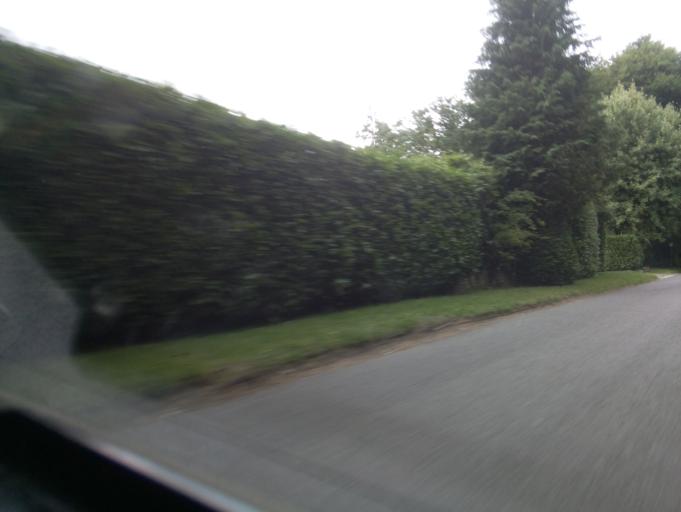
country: GB
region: England
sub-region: Gloucestershire
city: Shurdington
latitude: 51.7935
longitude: -2.1205
